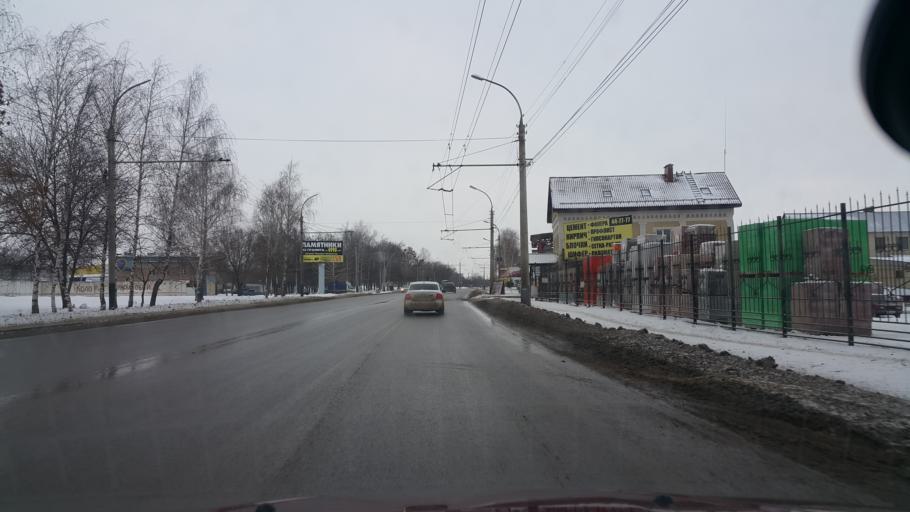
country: RU
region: Tambov
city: Tambov
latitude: 52.7344
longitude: 41.3950
